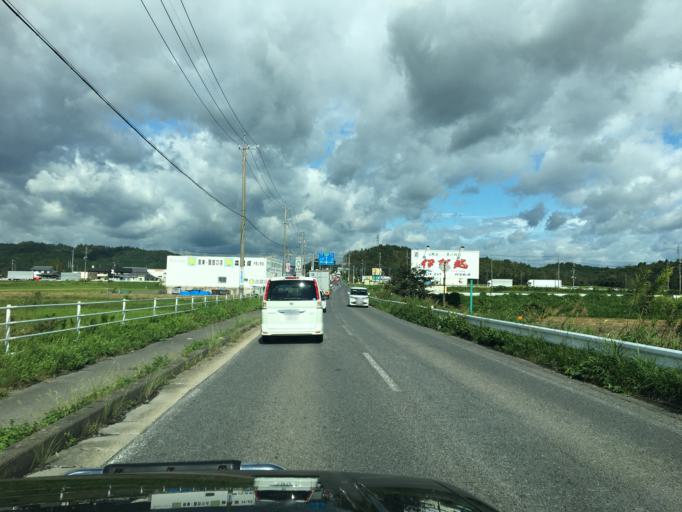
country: JP
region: Mie
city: Ueno-ebisumachi
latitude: 34.8090
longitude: 136.1866
